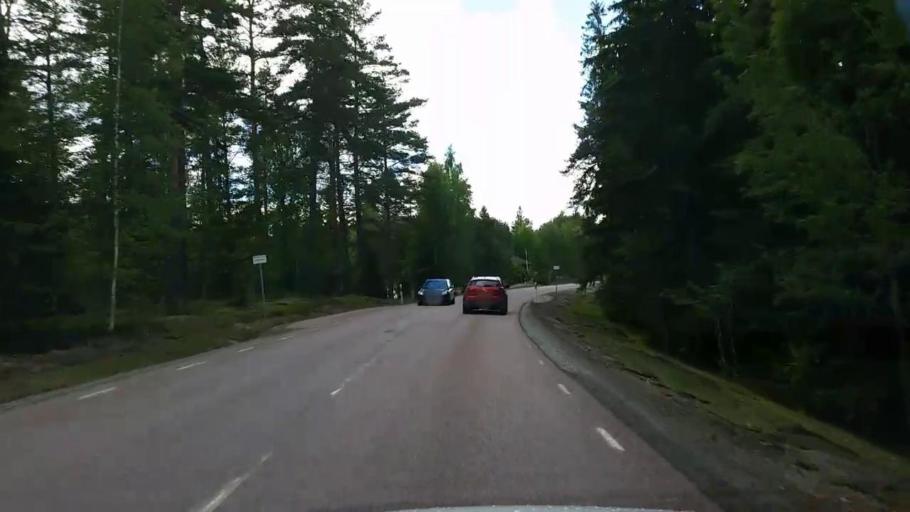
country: SE
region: Vaestmanland
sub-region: Fagersta Kommun
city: Fagersta
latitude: 59.8784
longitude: 15.8370
